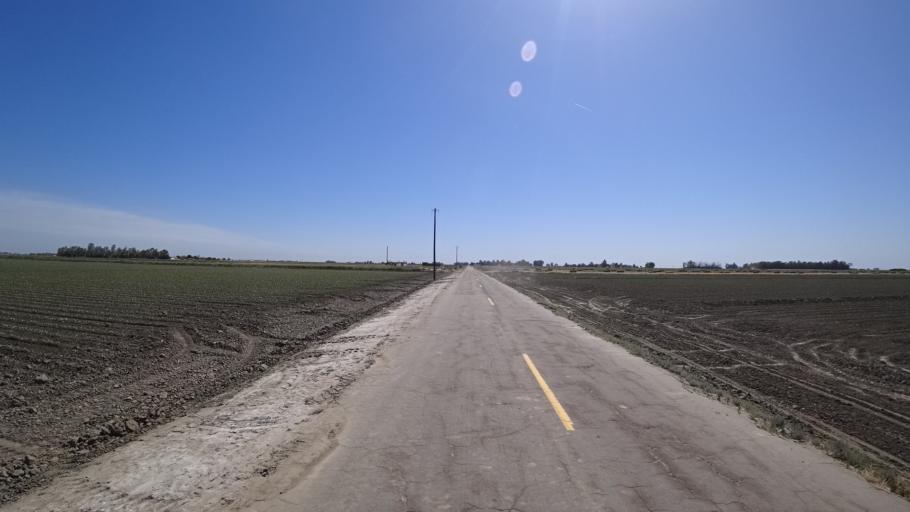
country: US
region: California
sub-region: Kings County
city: Stratford
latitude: 36.2041
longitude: -119.8129
